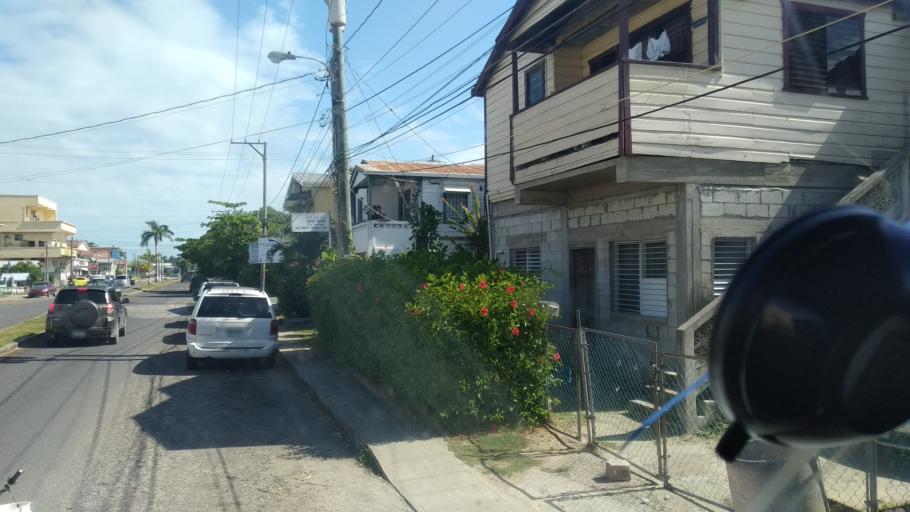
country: BZ
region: Belize
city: Belize City
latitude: 17.5070
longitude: -88.1943
